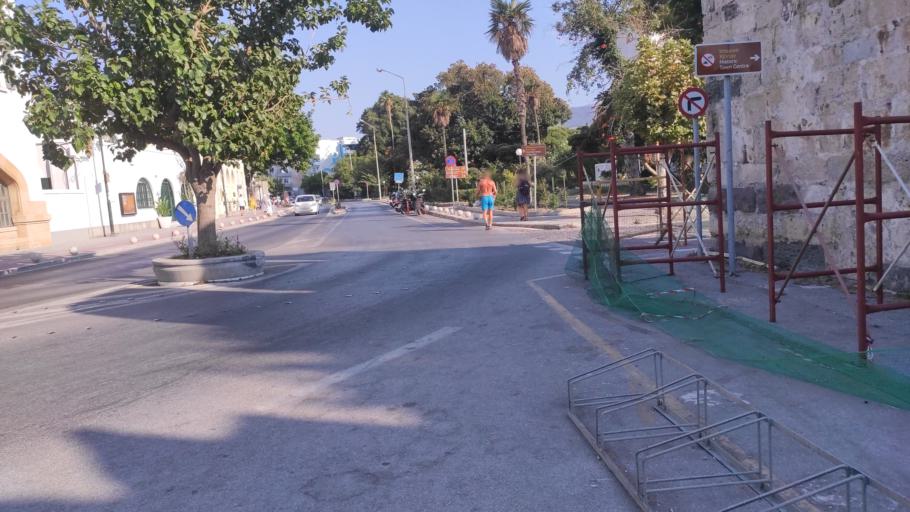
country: GR
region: South Aegean
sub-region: Nomos Dodekanisou
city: Kos
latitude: 36.8938
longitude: 27.2927
